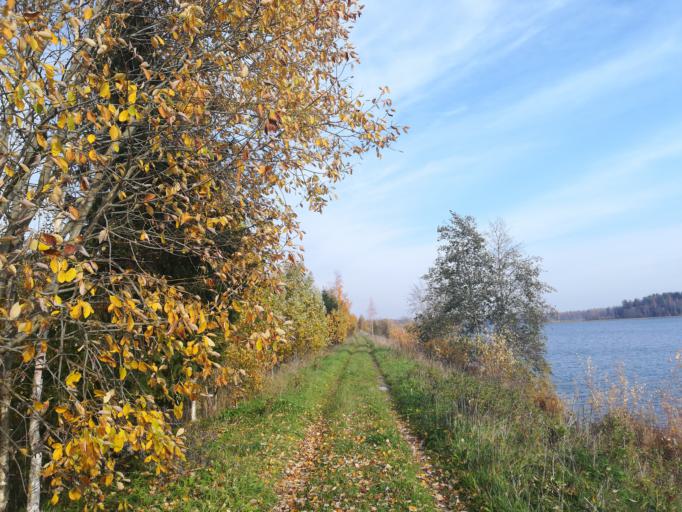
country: RU
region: Leningrad
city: Sista-Palkino
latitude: 59.5902
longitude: 28.8254
